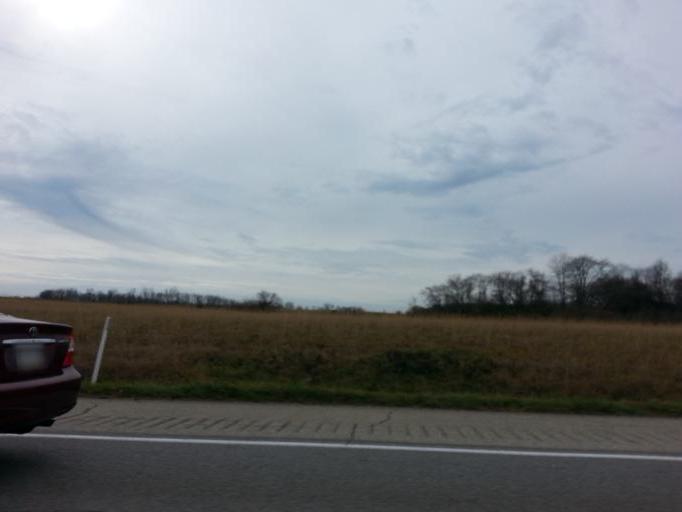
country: US
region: Indiana
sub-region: Decatur County
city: Greensburg
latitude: 39.3496
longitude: -85.4436
